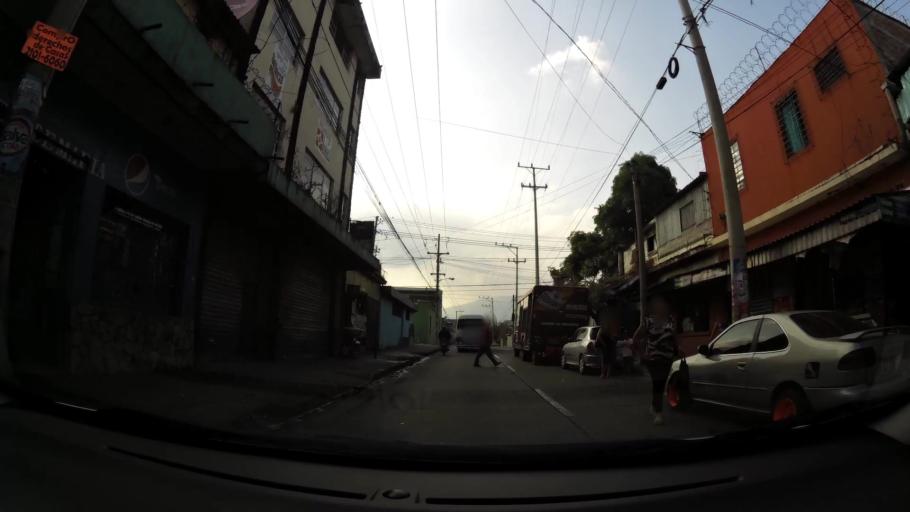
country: SV
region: San Salvador
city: San Salvador
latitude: 13.6962
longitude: -89.1830
